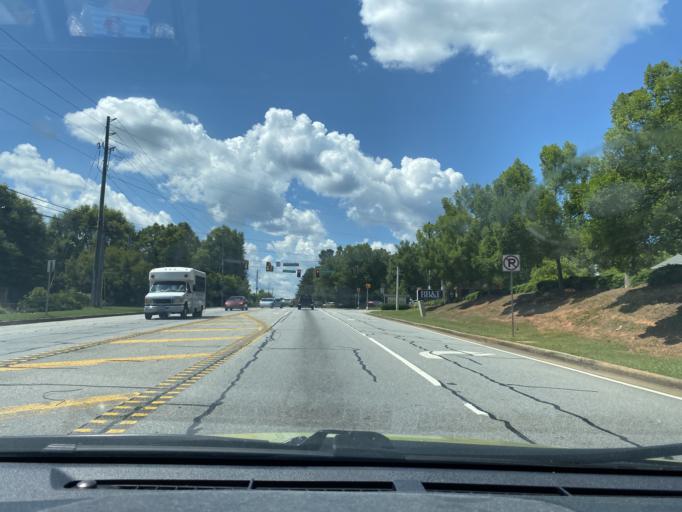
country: US
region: Georgia
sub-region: Fayette County
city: Peachtree City
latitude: 33.4121
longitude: -84.6827
